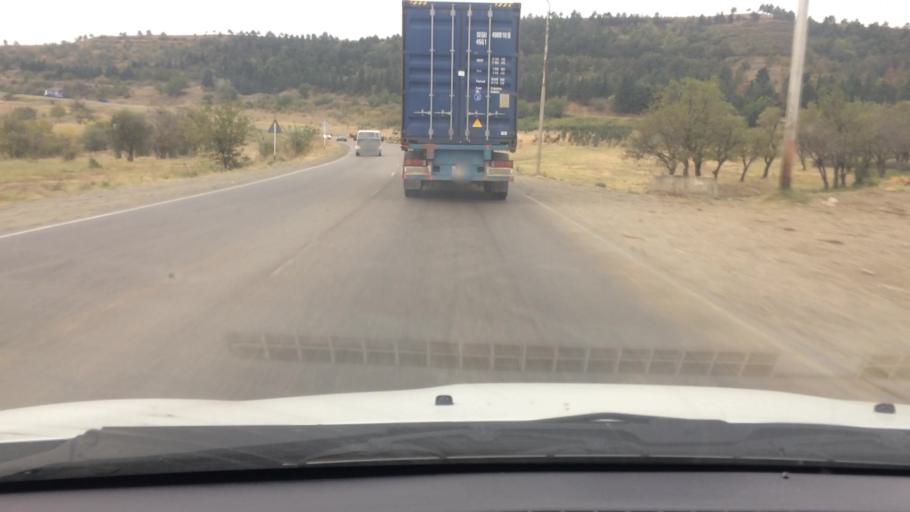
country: GE
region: T'bilisi
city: Tbilisi
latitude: 41.6034
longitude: 44.7799
